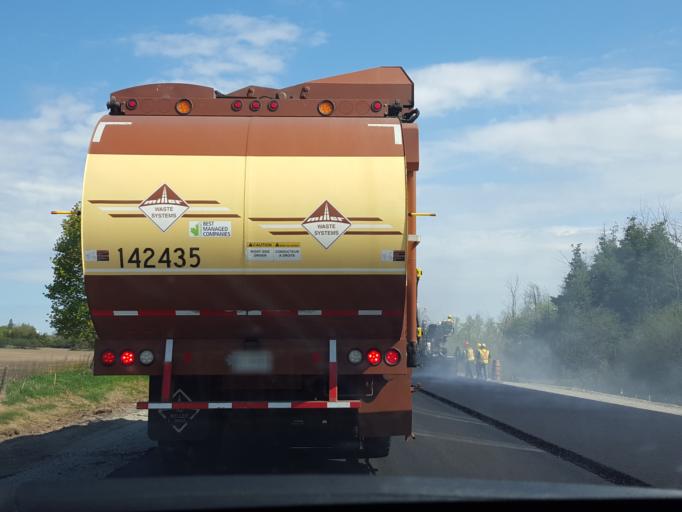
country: CA
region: Ontario
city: Uxbridge
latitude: 44.0764
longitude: -78.9366
